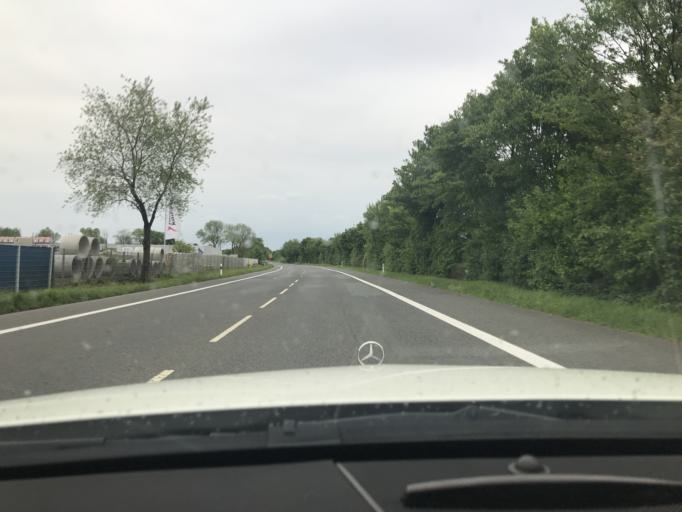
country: DE
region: North Rhine-Westphalia
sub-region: Regierungsbezirk Dusseldorf
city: Moers
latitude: 51.4576
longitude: 6.6114
